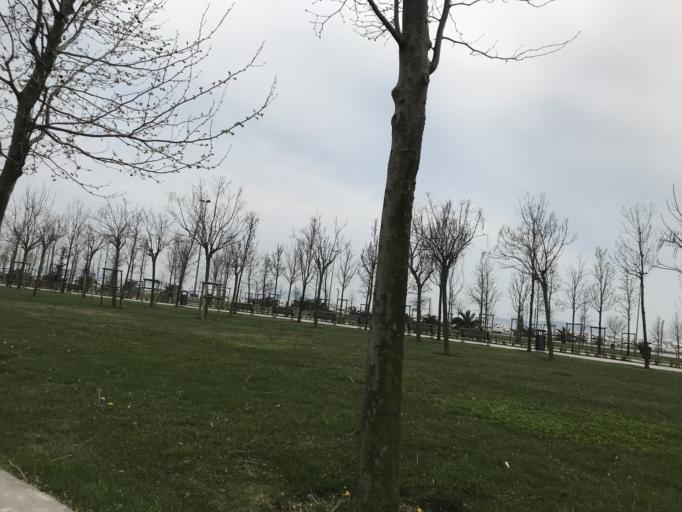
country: TR
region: Istanbul
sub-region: Atasehir
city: Atasehir
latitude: 40.9392
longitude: 29.1082
